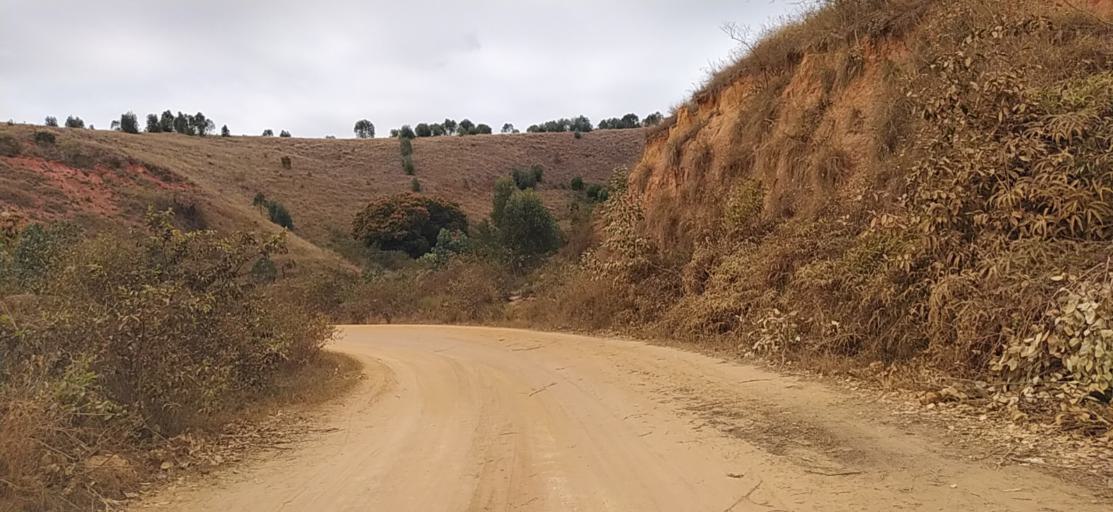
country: MG
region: Alaotra Mangoro
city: Ambatondrazaka
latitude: -18.0011
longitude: 48.2632
